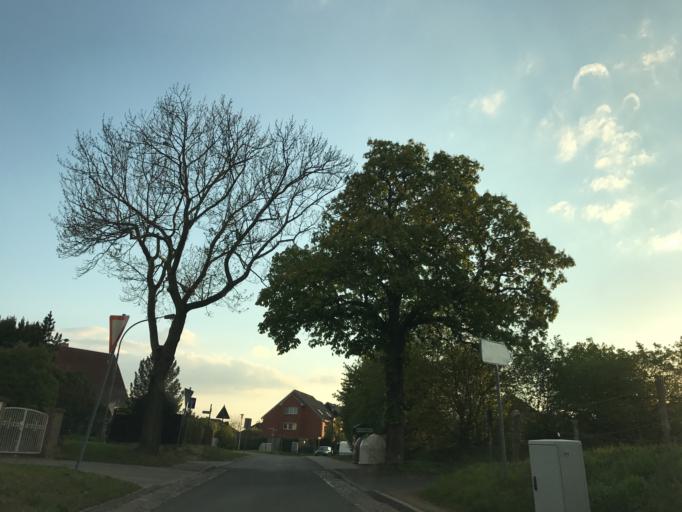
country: DE
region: Berlin
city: Staaken
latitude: 52.5074
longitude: 13.1140
